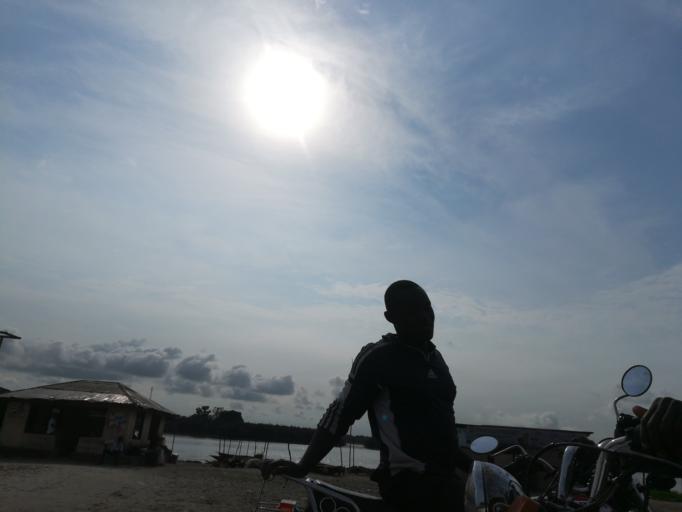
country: NG
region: Rivers
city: Okrika
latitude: 4.7405
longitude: 7.0897
